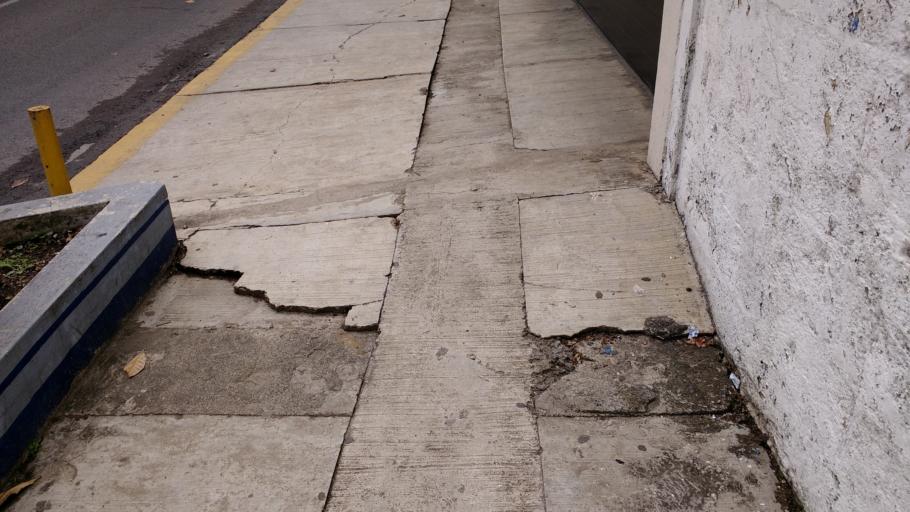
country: MX
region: Veracruz
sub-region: Xalapa
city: Xalapa de Enriquez
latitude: 19.5276
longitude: -96.9061
